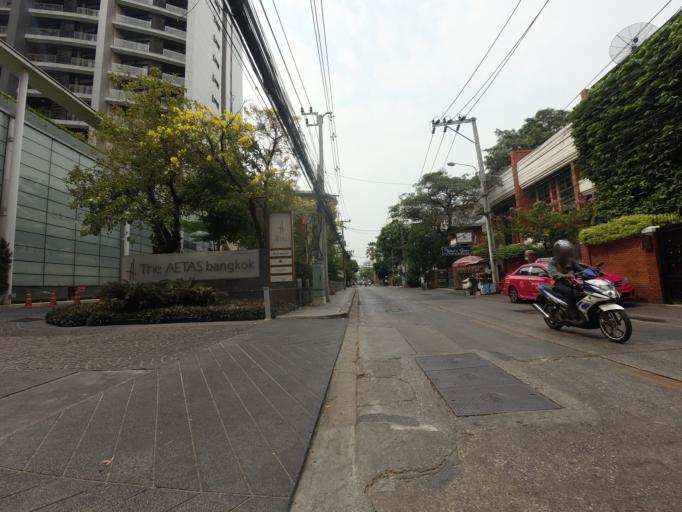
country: TH
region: Bangkok
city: Pathum Wan
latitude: 13.7384
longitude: 100.5491
